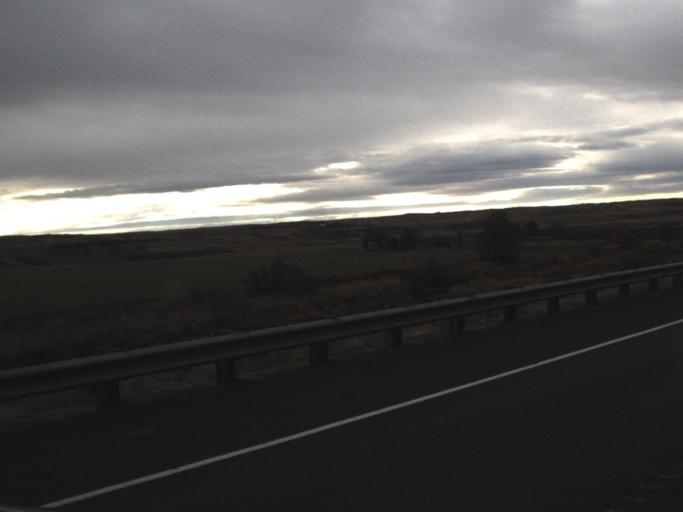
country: US
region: Washington
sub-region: Adams County
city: Ritzville
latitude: 46.7506
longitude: -118.1949
